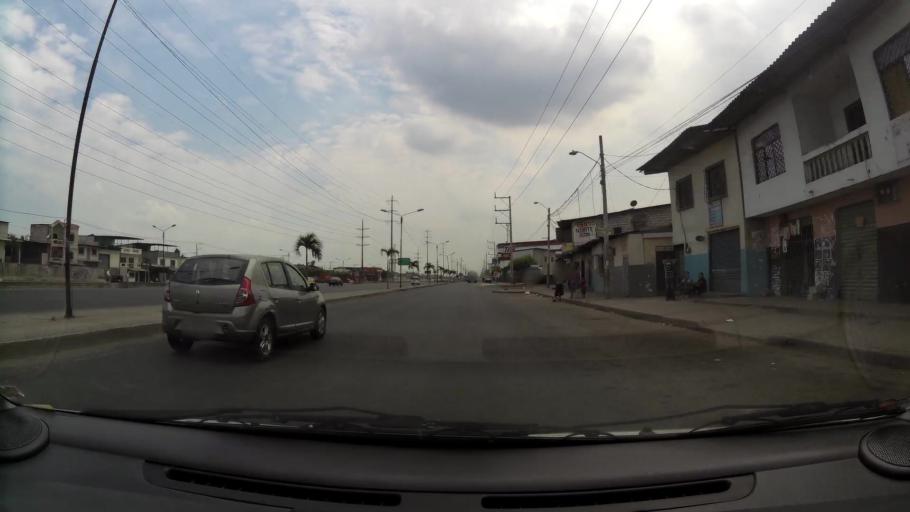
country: EC
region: Guayas
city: Guayaquil
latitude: -2.2392
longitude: -79.9223
